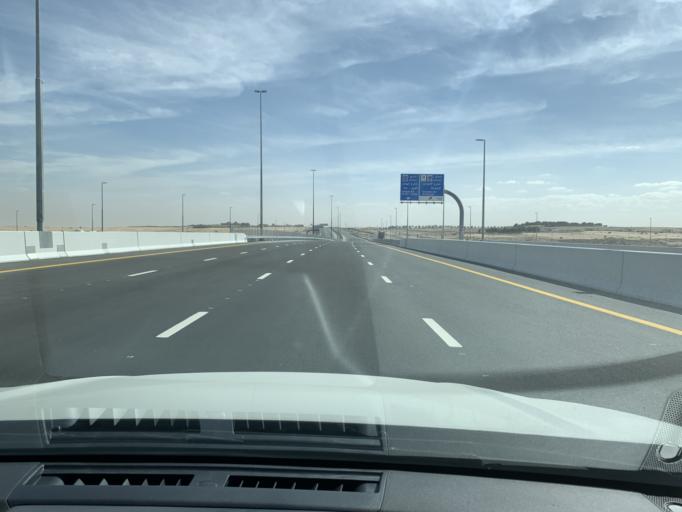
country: AE
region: Dubai
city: Dubai
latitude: 24.9538
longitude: 55.2346
